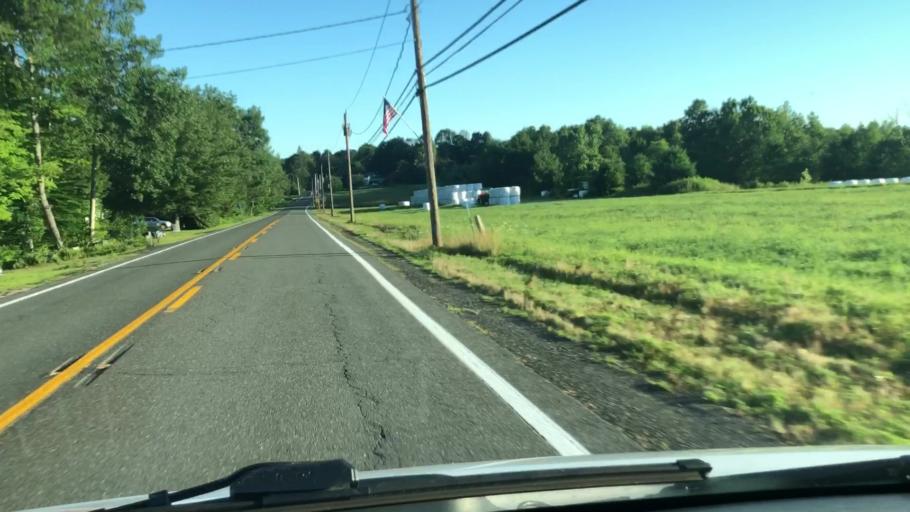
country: US
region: Massachusetts
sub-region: Hampshire County
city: Chesterfield
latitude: 42.3910
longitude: -72.9326
